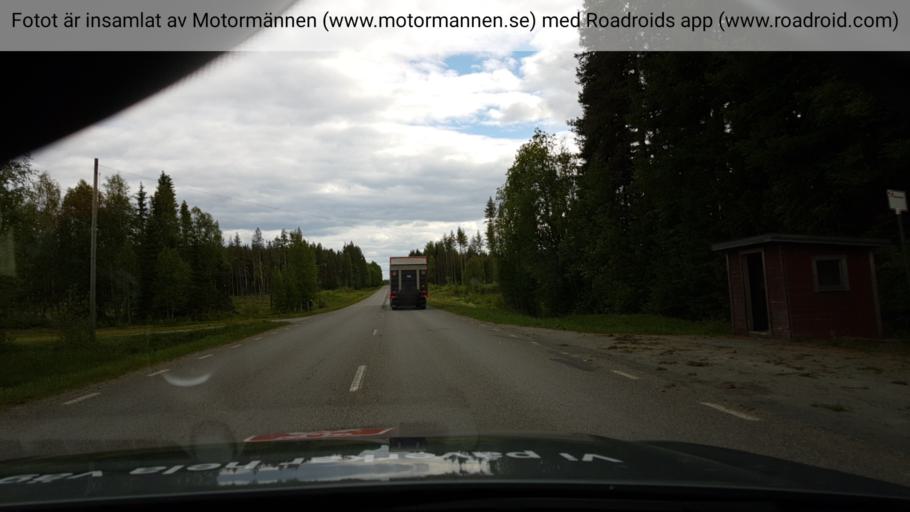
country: SE
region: Jaemtland
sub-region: Stroemsunds Kommun
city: Stroemsund
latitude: 63.8776
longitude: 15.5451
